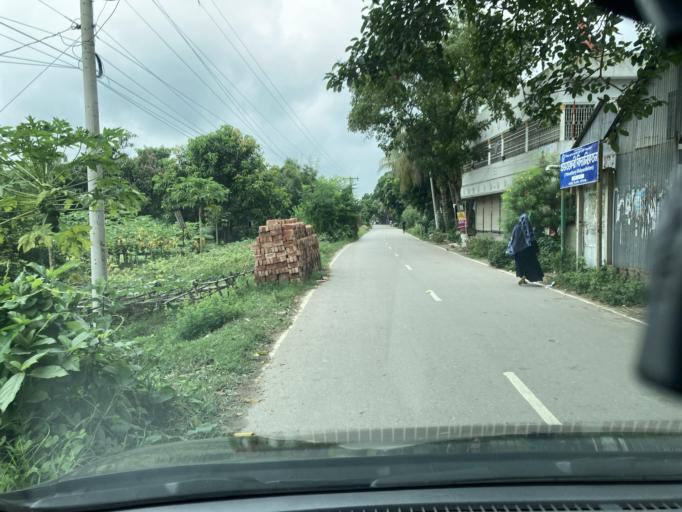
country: BD
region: Dhaka
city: Azimpur
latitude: 23.7699
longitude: 90.2052
